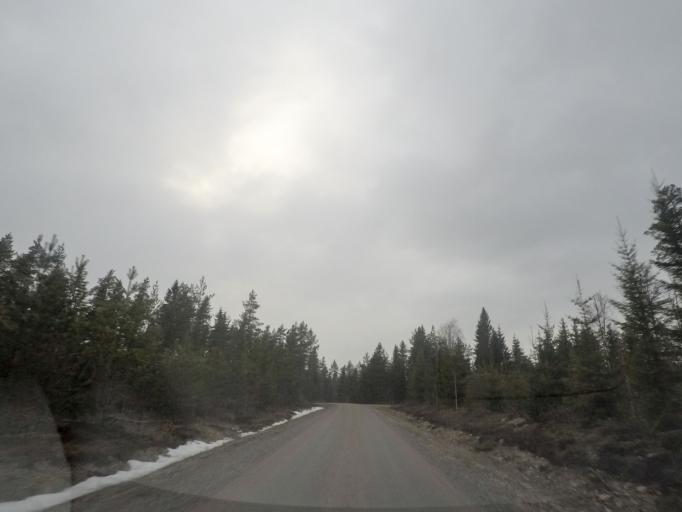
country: SE
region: OErebro
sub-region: Hallefors Kommun
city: Haellefors
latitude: 60.0345
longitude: 14.5348
